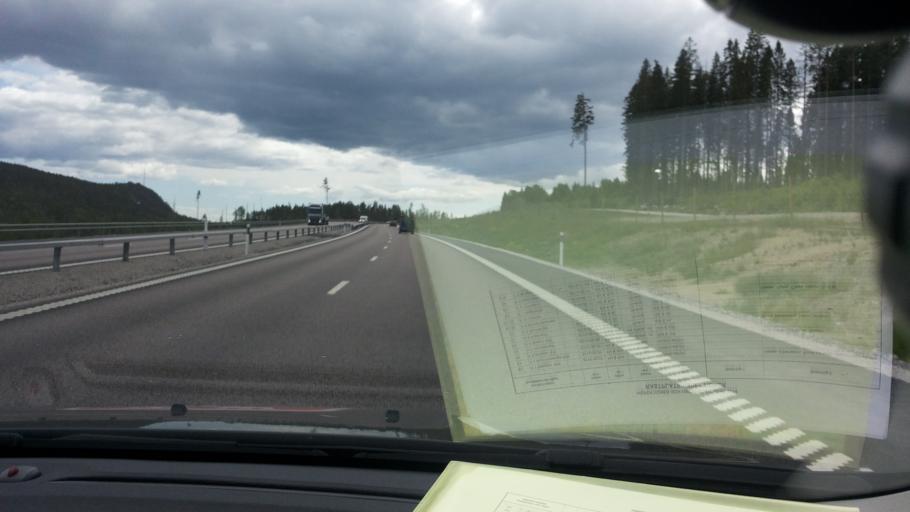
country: SE
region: Vaesternorrland
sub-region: Sundsvalls Kommun
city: Stockvik
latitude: 62.3173
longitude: 17.3394
